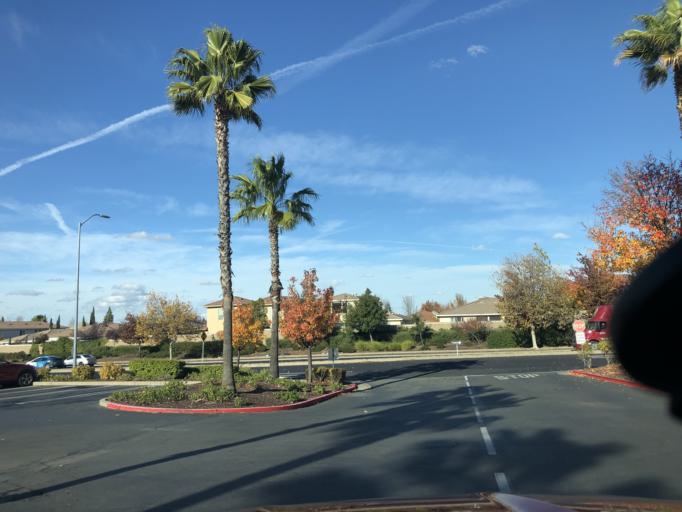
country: US
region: California
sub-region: Placer County
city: Roseville
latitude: 38.7897
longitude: -121.2856
